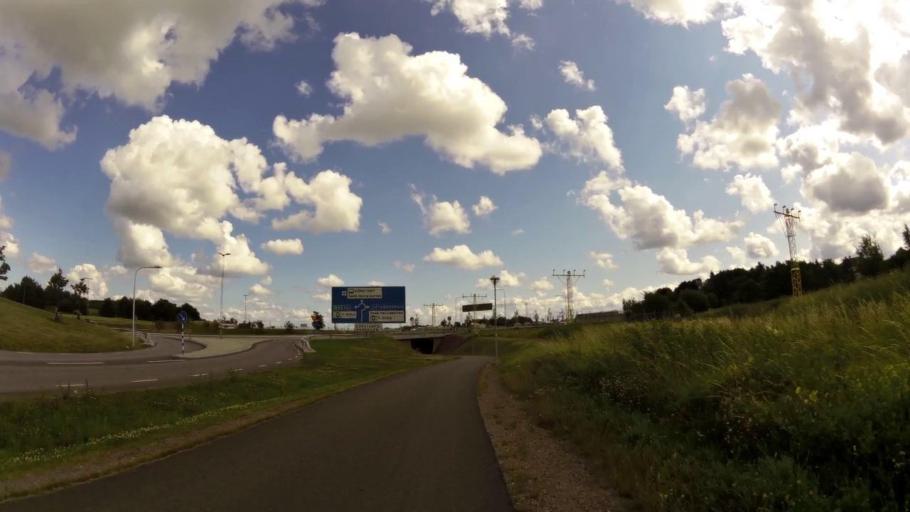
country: SE
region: OEstergoetland
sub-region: Linkopings Kommun
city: Linkoping
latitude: 58.4127
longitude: 15.6519
